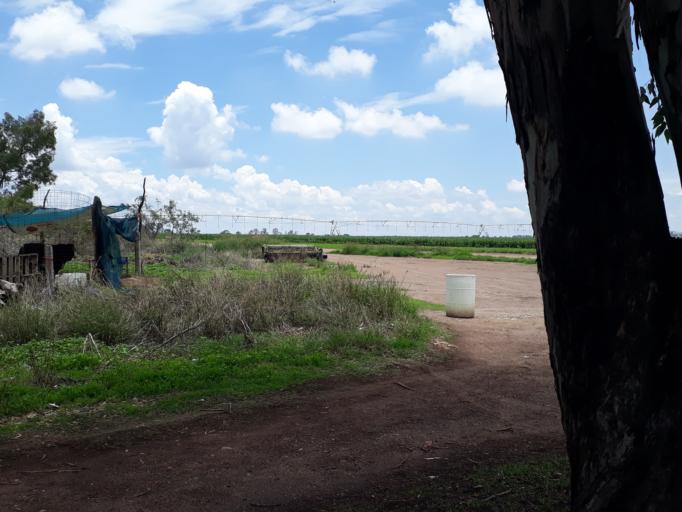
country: MX
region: Aguascalientes
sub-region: Aguascalientes
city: La Loma de los Negritos
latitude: 21.8249
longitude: -102.3265
